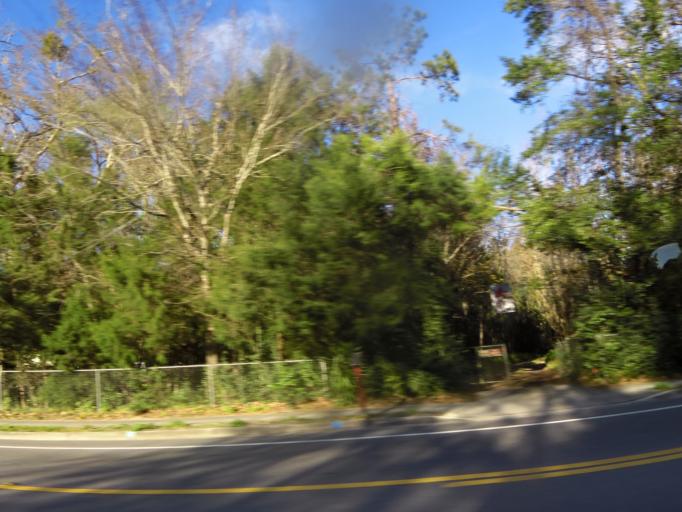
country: US
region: Florida
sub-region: Duval County
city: Jacksonville
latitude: 30.4598
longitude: -81.6141
